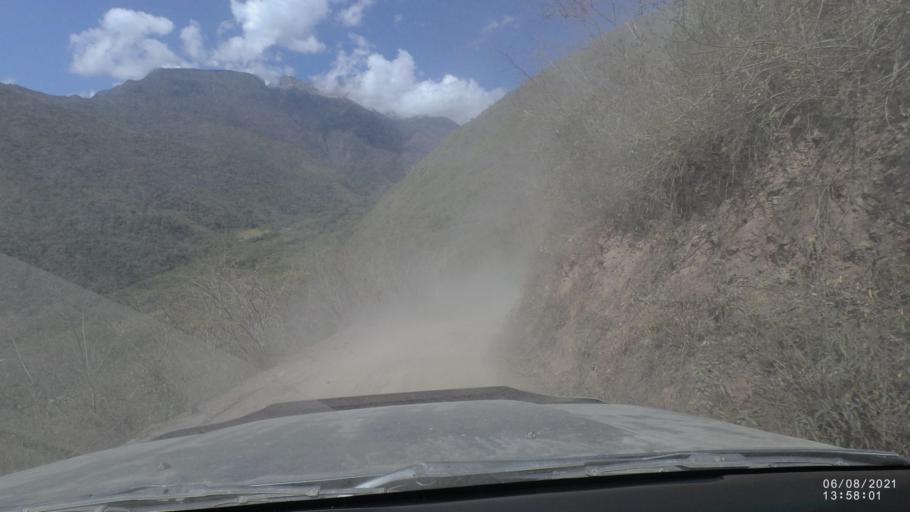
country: BO
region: La Paz
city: Quime
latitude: -16.6455
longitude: -66.7276
